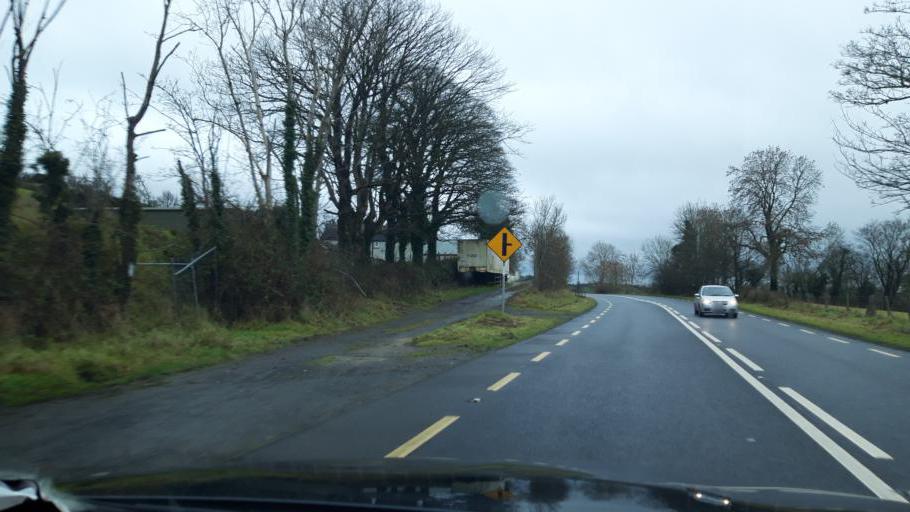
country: IE
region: Ulster
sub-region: County Monaghan
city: Castleblayney
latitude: 54.0948
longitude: -6.7024
